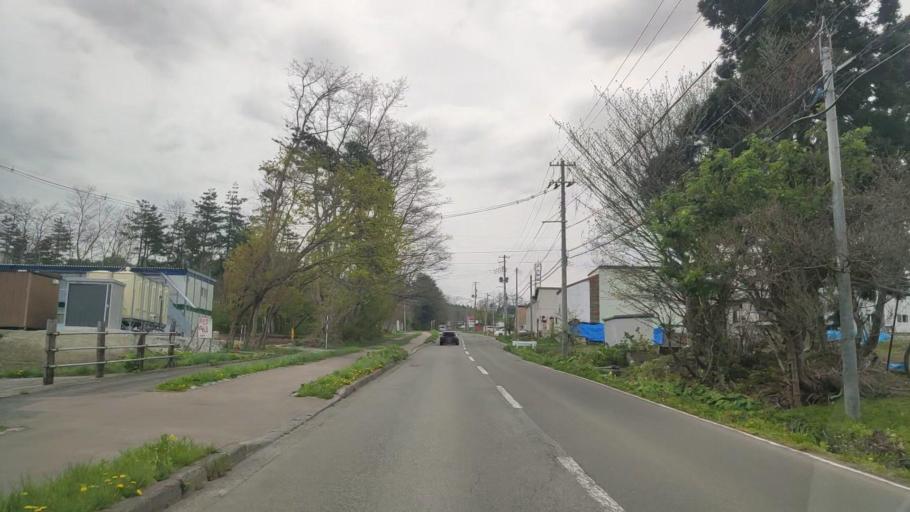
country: JP
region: Aomori
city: Aomori Shi
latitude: 40.7702
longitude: 140.7990
